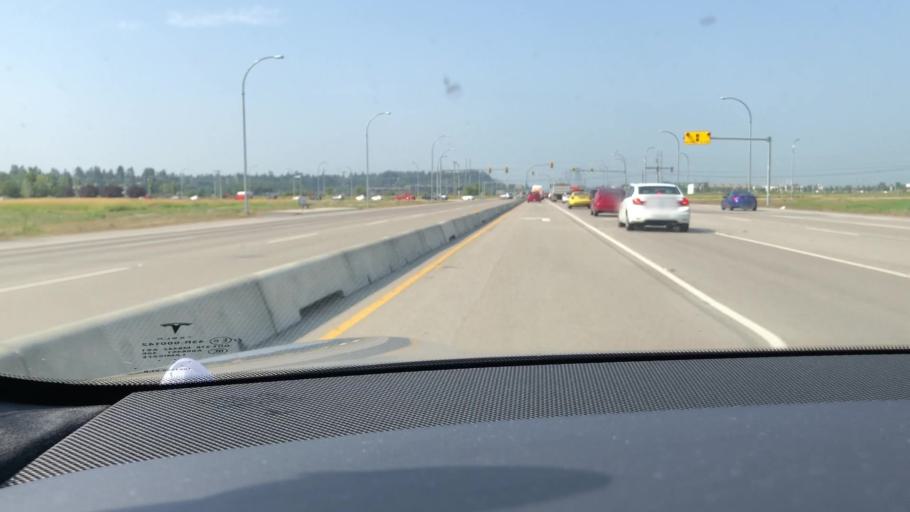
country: CA
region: British Columbia
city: Ladner
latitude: 49.0439
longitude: -123.0664
